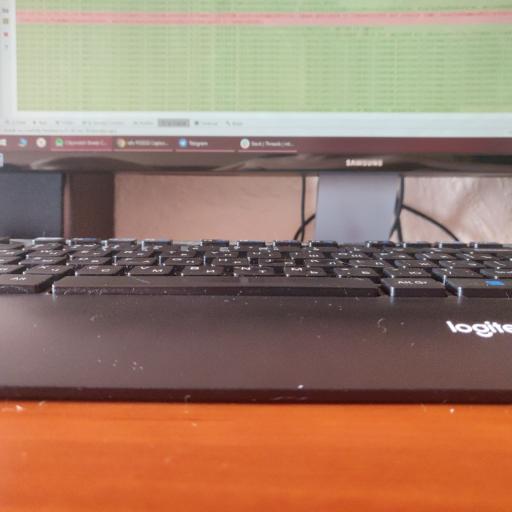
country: AX
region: Alands skaergard
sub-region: Vardoe
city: Vardoe
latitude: 60.8030
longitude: 20.4440
